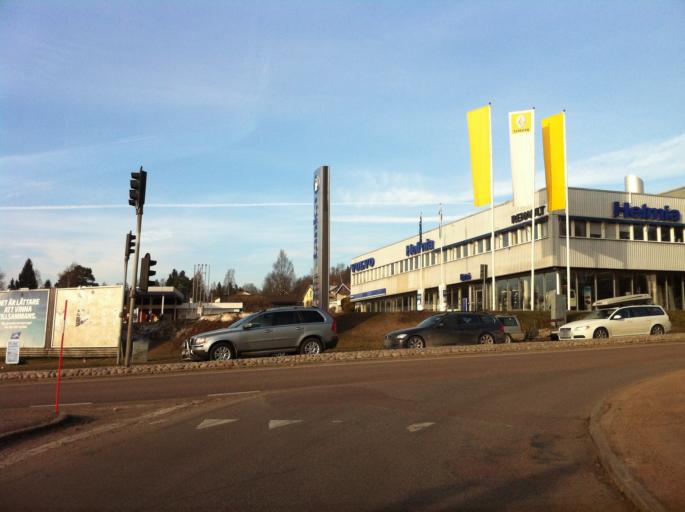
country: SE
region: Vaermland
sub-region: Filipstads Kommun
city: Filipstad
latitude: 59.7140
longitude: 14.1742
